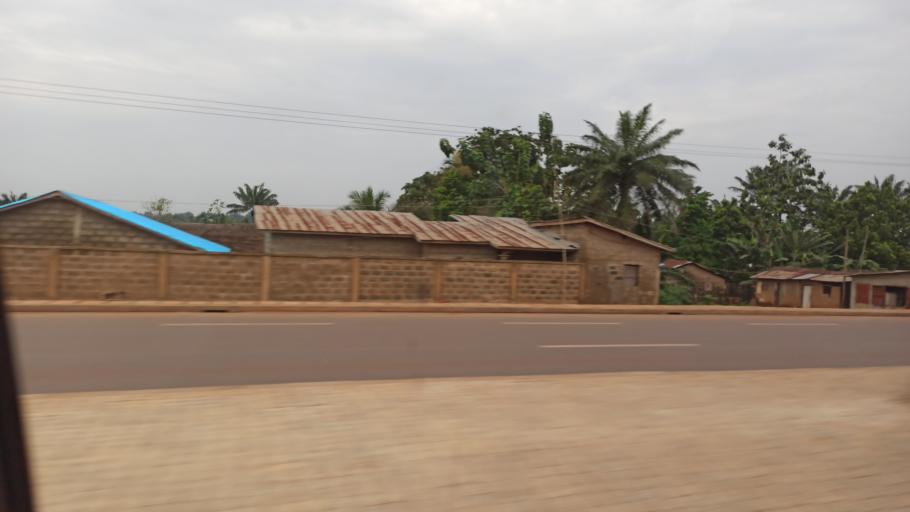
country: BJ
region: Queme
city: Porto-Novo
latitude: 6.5282
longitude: 2.6006
